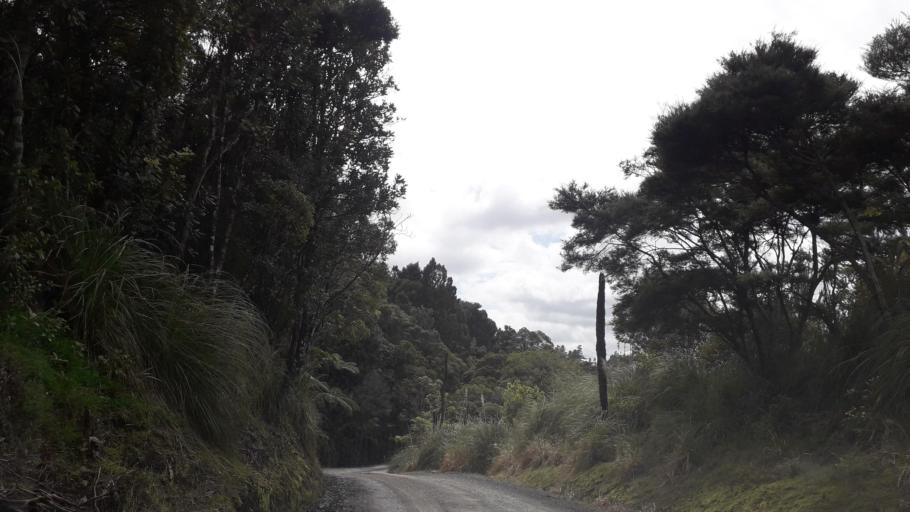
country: NZ
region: Northland
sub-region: Far North District
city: Kaitaia
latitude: -35.1982
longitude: 173.2824
